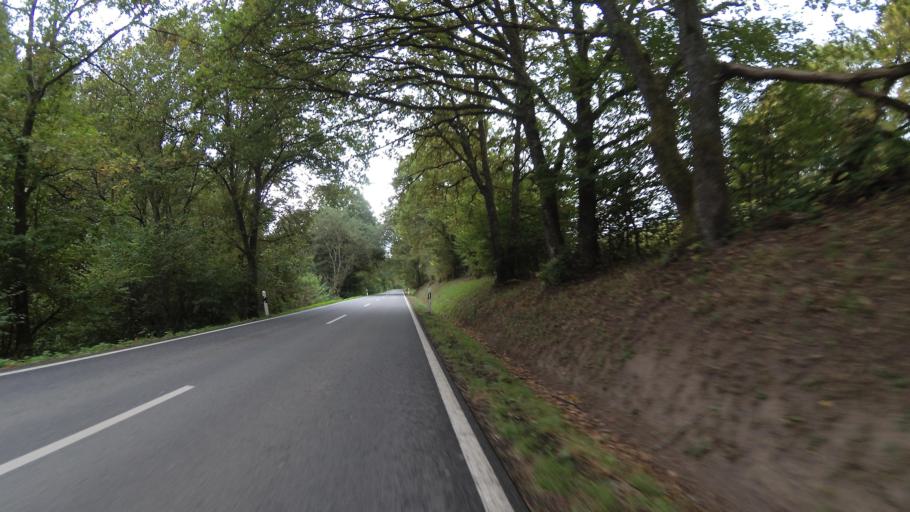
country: DE
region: Rheinland-Pfalz
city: Breitenbach
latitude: 49.4523
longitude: 7.2638
